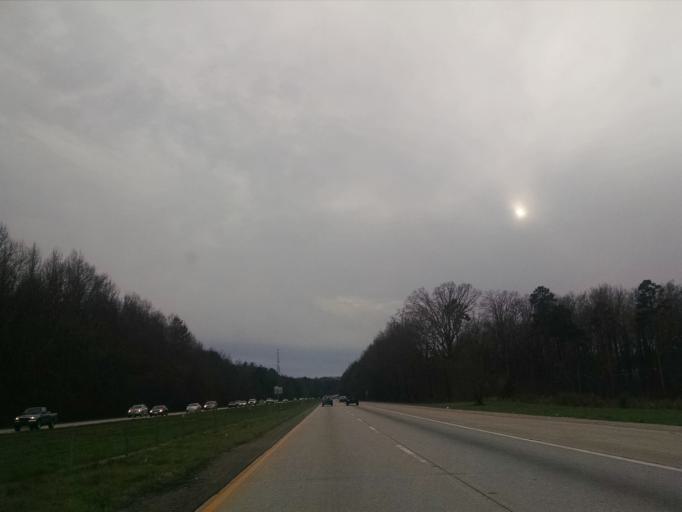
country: US
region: Georgia
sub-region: Hall County
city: Oakwood
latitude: 34.2069
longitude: -83.8888
